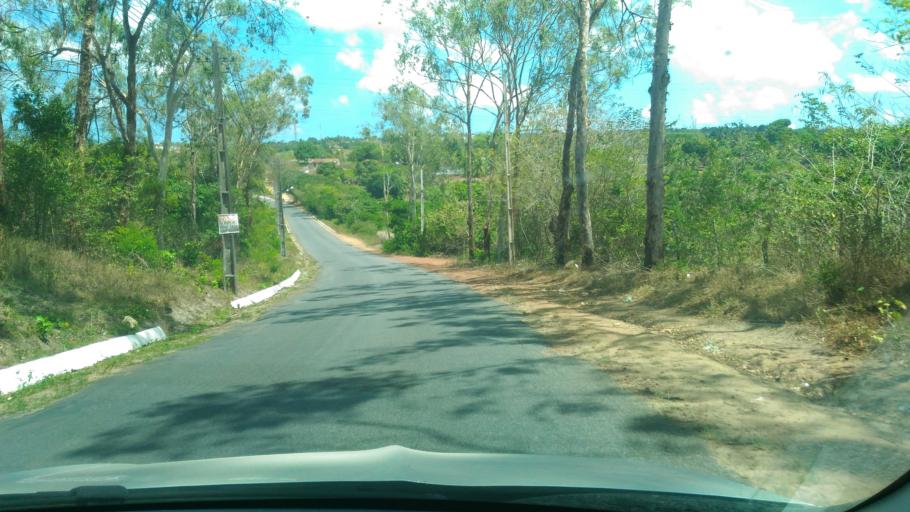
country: BR
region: Paraiba
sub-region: Conde
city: Conde
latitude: -7.2631
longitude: -34.9254
